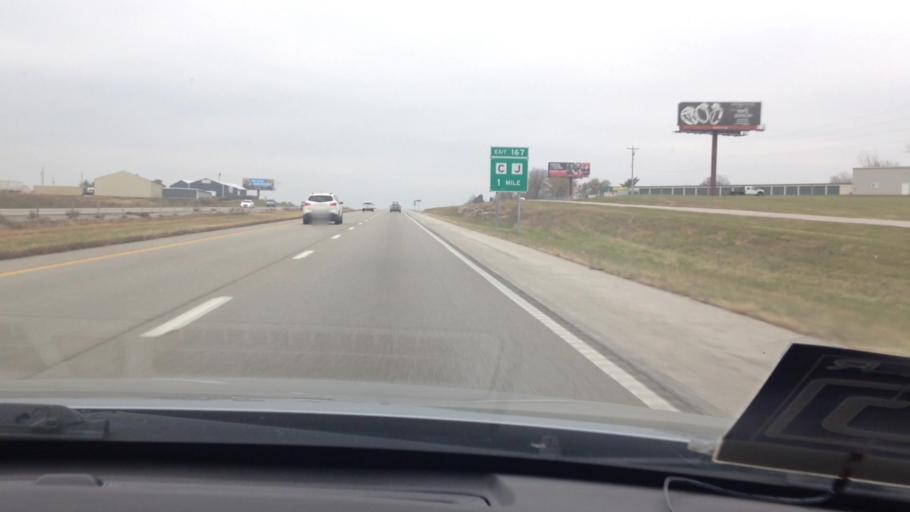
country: US
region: Missouri
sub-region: Cass County
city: Peculiar
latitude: 38.7064
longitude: -94.4391
